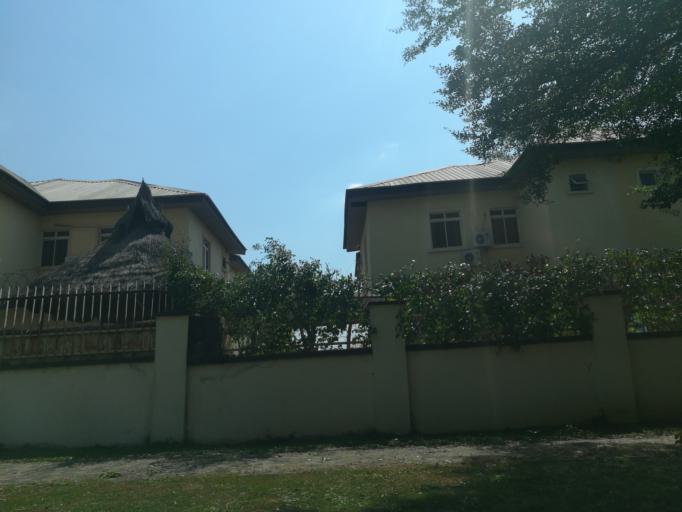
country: NG
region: Abuja Federal Capital Territory
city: Abuja
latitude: 9.0680
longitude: 7.4243
